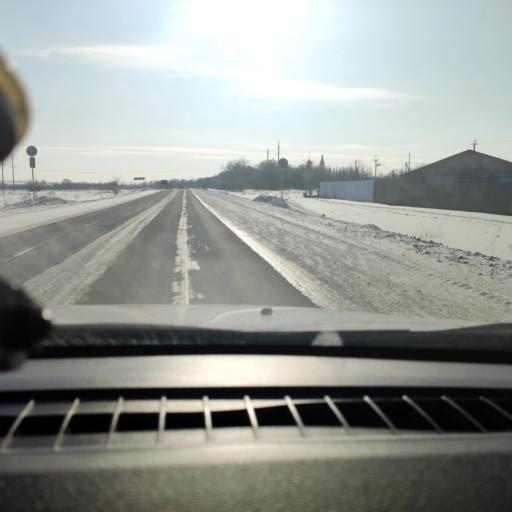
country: RU
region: Samara
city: Smyshlyayevka
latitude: 53.1778
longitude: 50.4613
